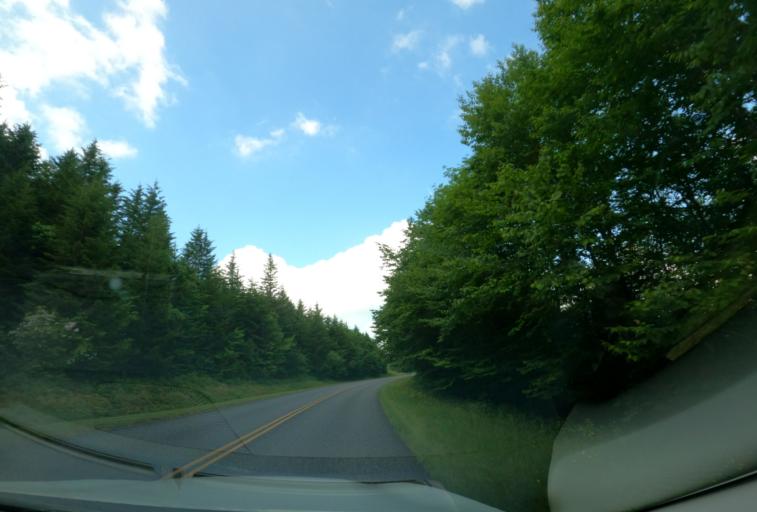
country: US
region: North Carolina
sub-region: Haywood County
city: Hazelwood
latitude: 35.3789
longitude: -83.0131
